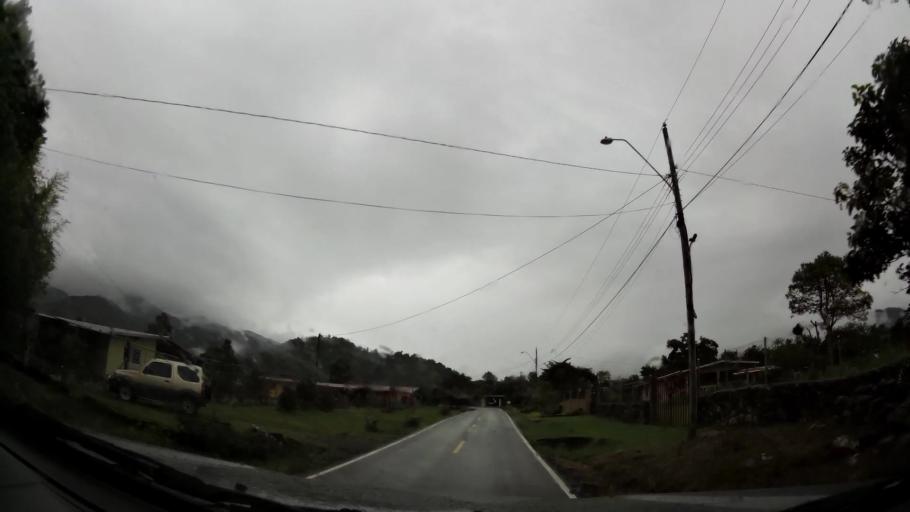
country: PA
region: Chiriqui
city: Volcan
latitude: 8.7929
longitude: -82.6492
